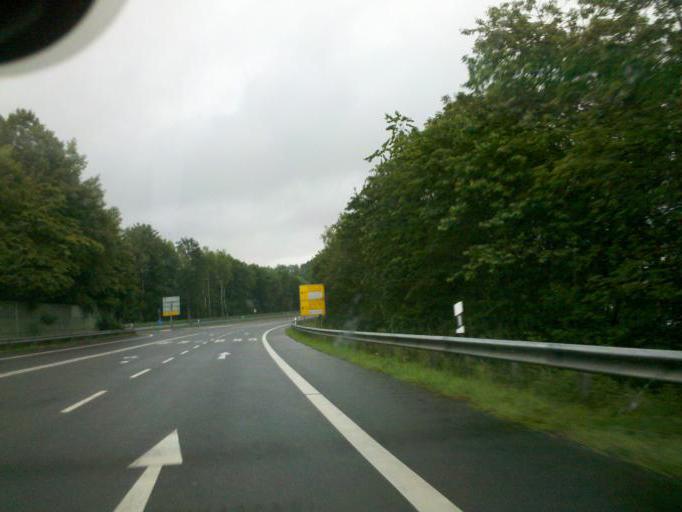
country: DE
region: North Rhine-Westphalia
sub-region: Regierungsbezirk Arnsberg
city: Olpe
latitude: 51.0471
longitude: 7.8563
